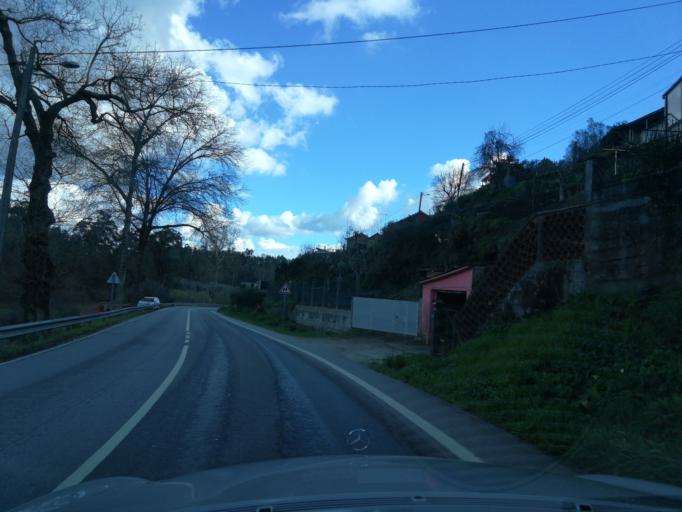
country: PT
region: Viana do Castelo
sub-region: Ponte de Lima
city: Ponte de Lima
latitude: 41.6920
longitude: -8.5315
